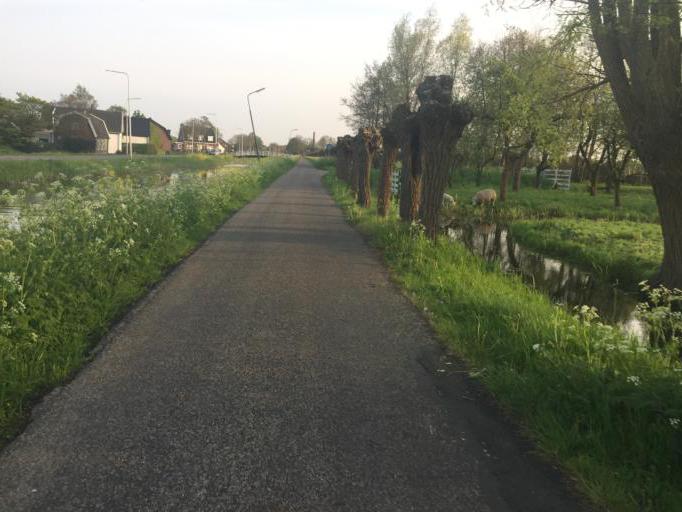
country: NL
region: Utrecht
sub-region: Gemeente Woerden
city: Woerden
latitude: 52.1038
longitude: 4.8941
